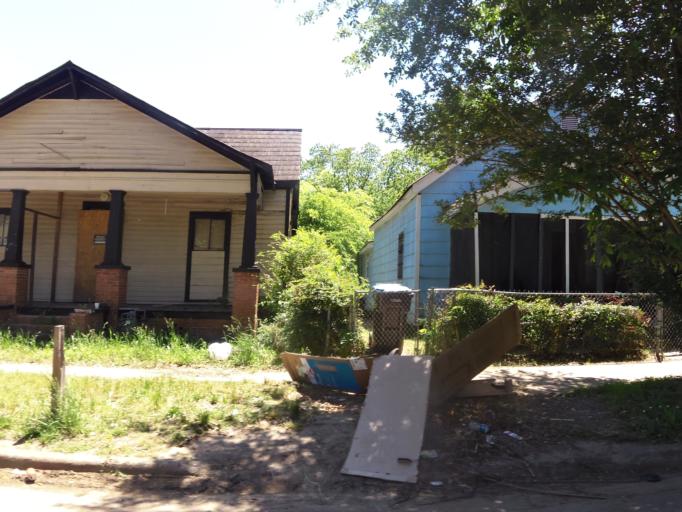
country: US
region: Georgia
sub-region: Richmond County
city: Augusta
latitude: 33.4592
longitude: -81.9792
